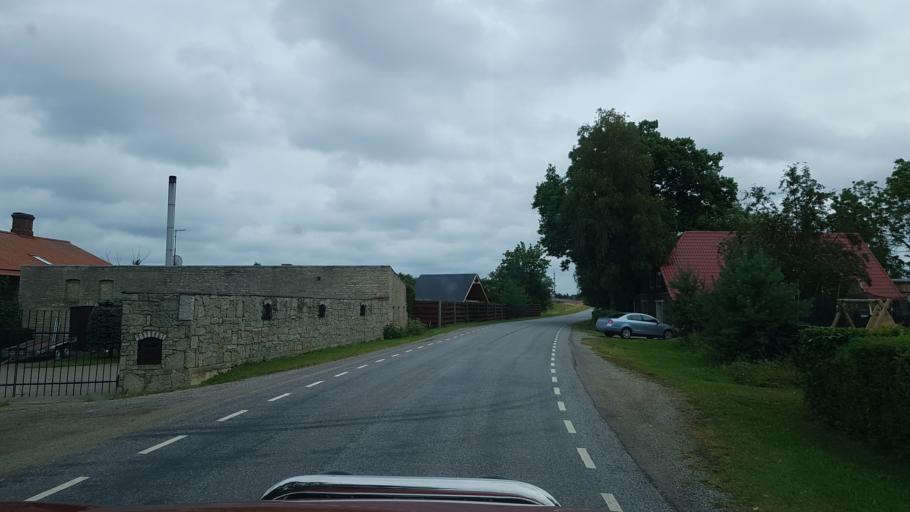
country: EE
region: Ida-Virumaa
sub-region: Puessi linn
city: Pussi
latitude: 59.3786
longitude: 27.0383
